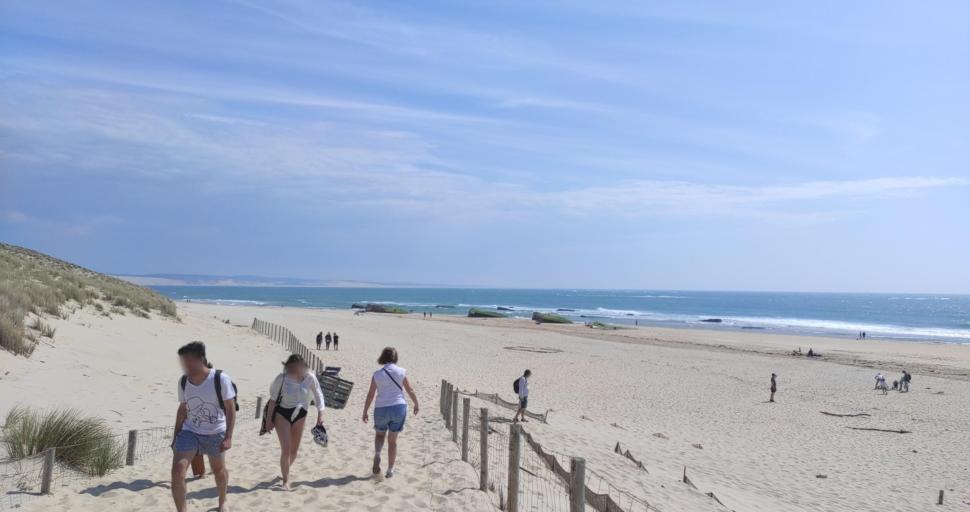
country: FR
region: Aquitaine
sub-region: Departement de la Gironde
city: Arcachon
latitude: 44.6265
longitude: -1.2572
